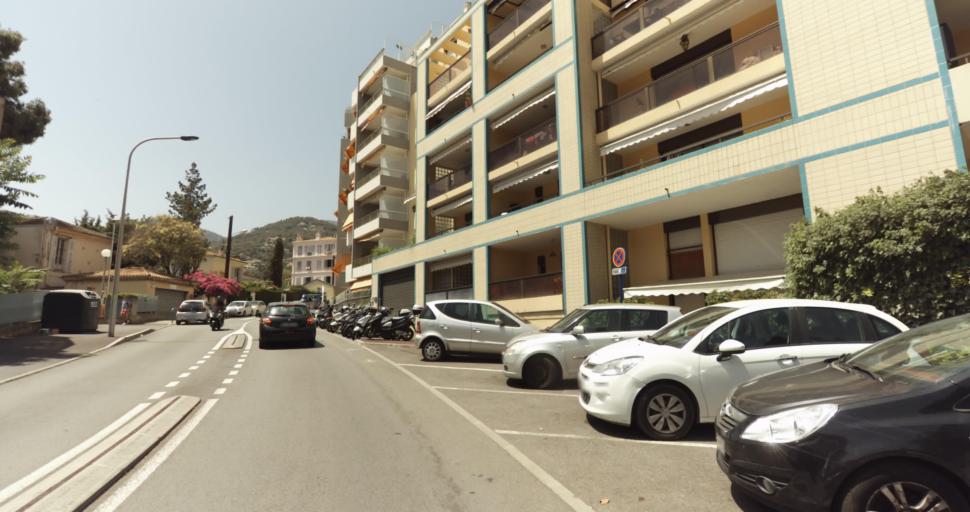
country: FR
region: Provence-Alpes-Cote d'Azur
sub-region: Departement des Alpes-Maritimes
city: Roquebrune-Cap-Martin
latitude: 43.7675
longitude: 7.4851
